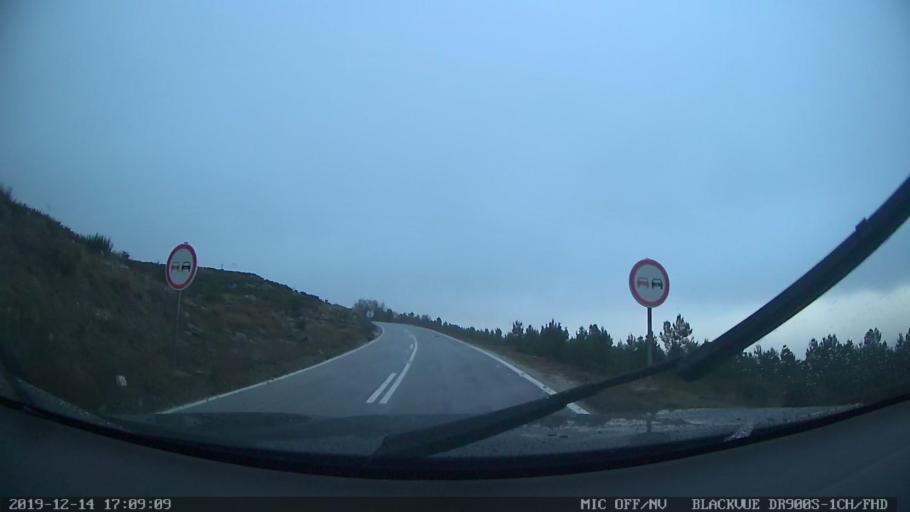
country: PT
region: Vila Real
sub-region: Vila Pouca de Aguiar
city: Vila Pouca de Aguiar
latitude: 41.4740
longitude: -7.6039
